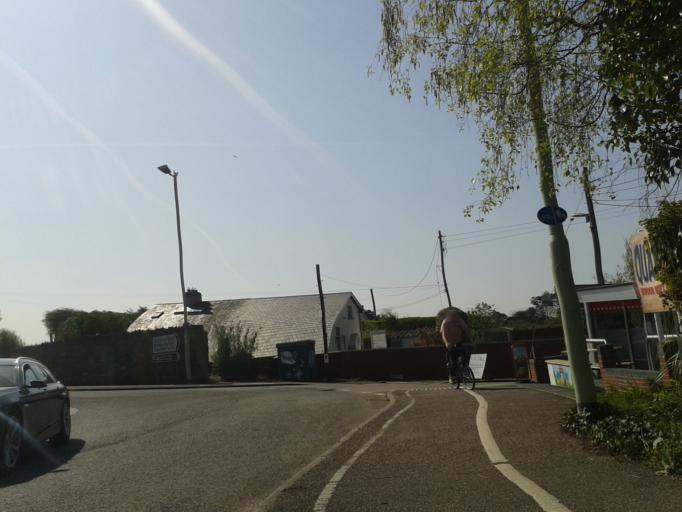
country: GB
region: England
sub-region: Devon
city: Braunton
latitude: 51.1016
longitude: -4.1626
